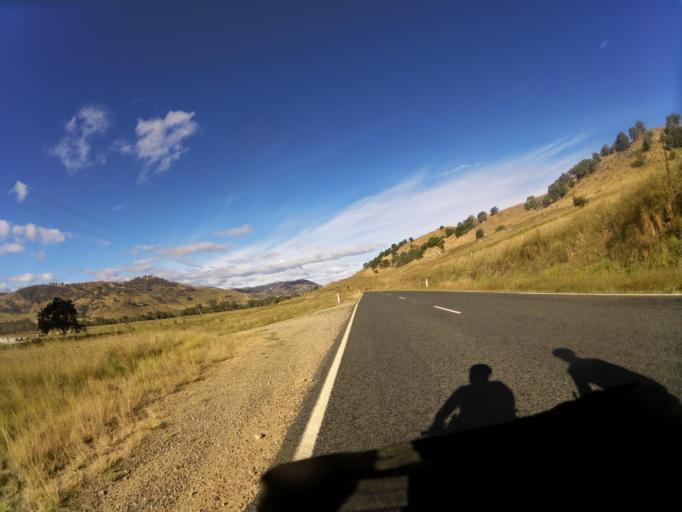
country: AU
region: New South Wales
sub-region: Greater Hume Shire
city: Holbrook
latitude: -35.9654
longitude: 147.7547
